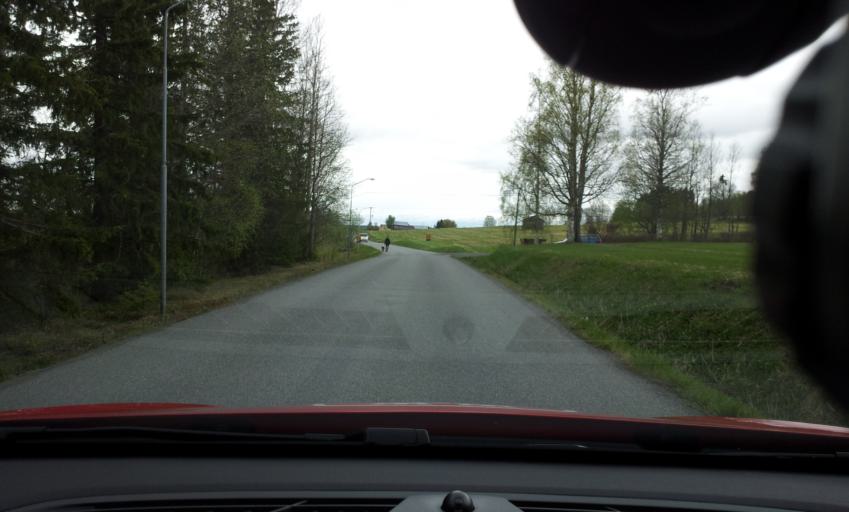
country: SE
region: Jaemtland
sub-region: OEstersunds Kommun
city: Brunflo
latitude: 63.0336
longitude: 14.8141
